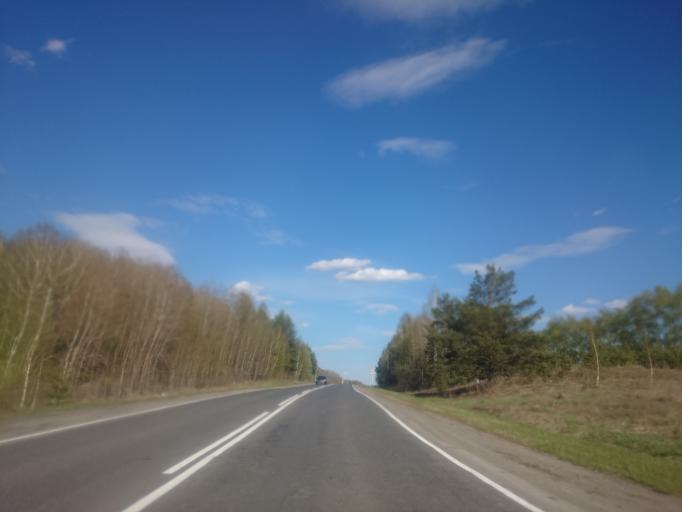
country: RU
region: Sverdlovsk
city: Lesnoy
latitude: 57.6200
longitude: 63.2264
